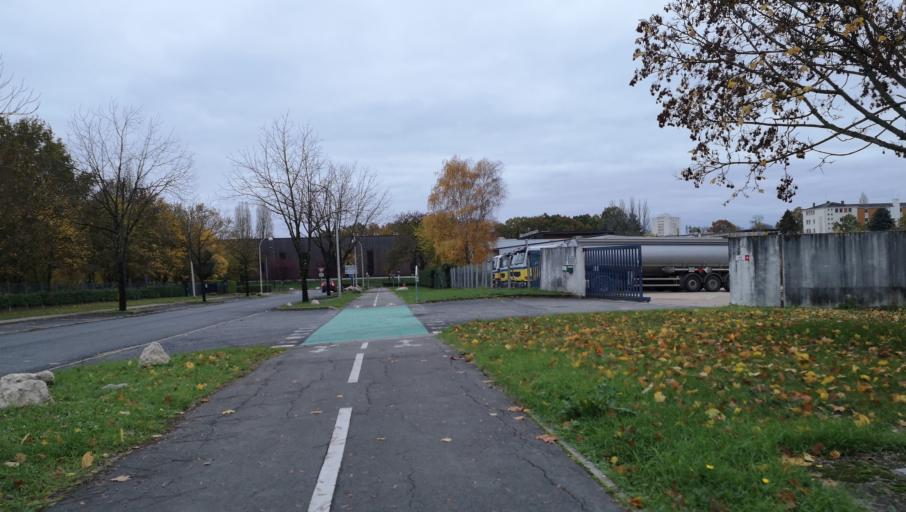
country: FR
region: Centre
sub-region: Departement du Loiret
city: Semoy
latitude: 47.9139
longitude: 1.9466
